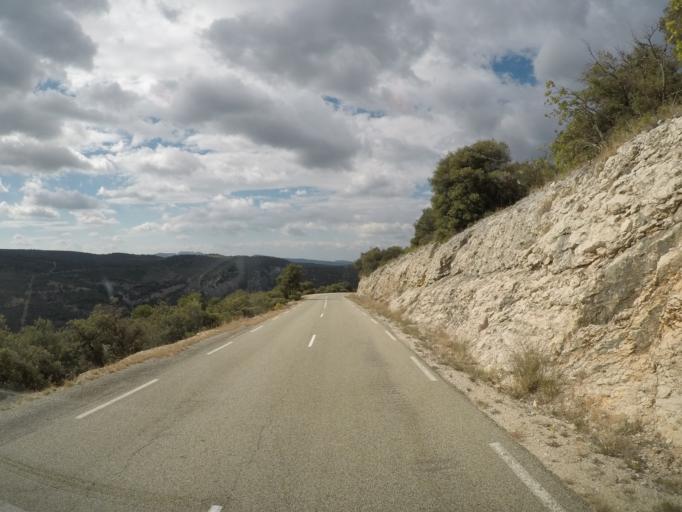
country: FR
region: Rhone-Alpes
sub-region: Departement de la Drome
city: Buis-les-Baronnies
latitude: 44.2220
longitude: 5.2074
